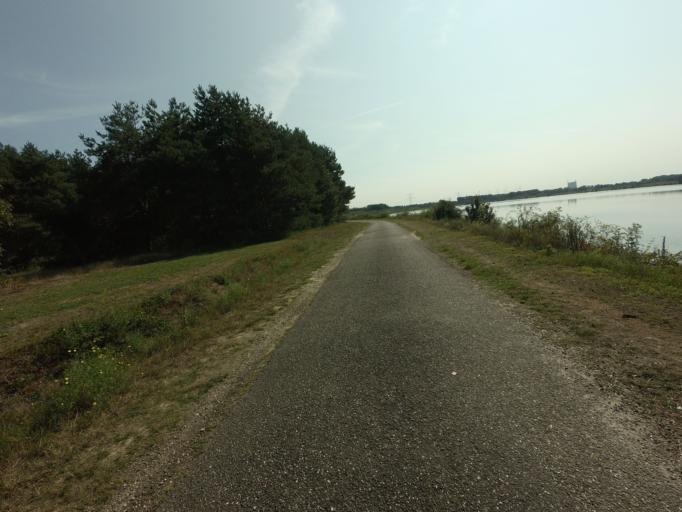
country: NL
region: Limburg
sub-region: Gemeente Leudal
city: Heythuysen
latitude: 51.1969
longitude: 5.9019
